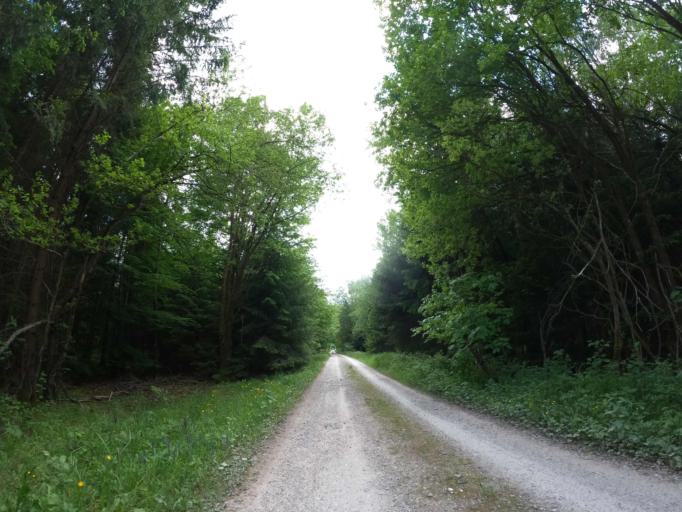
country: DE
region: Bavaria
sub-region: Upper Bavaria
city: Sauerlach
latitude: 47.9786
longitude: 11.6786
